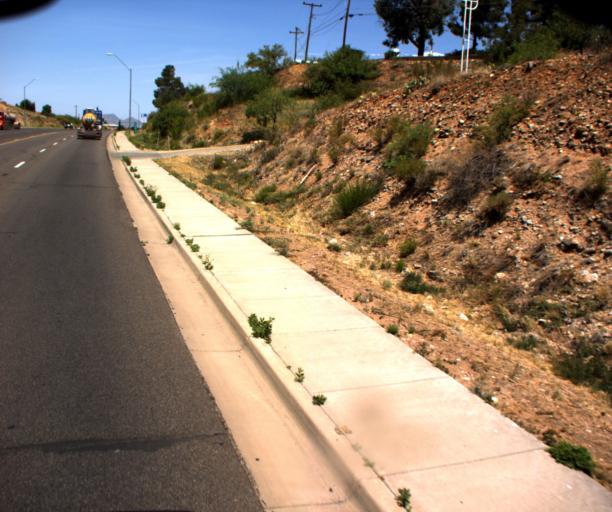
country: US
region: Arizona
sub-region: Gila County
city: Globe
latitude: 33.3820
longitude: -110.7531
